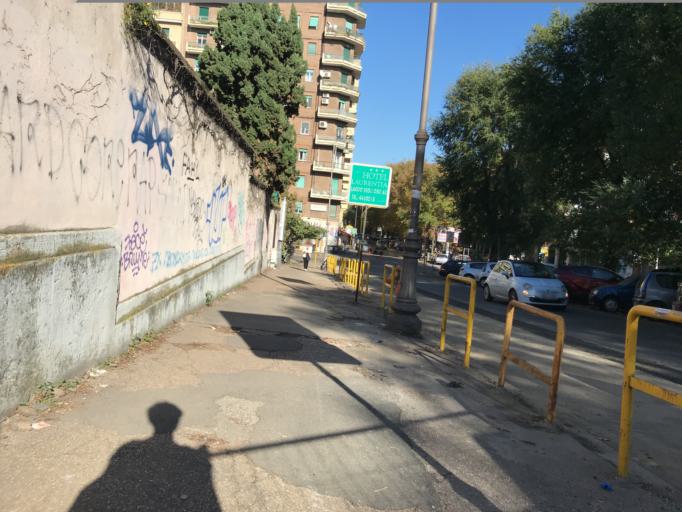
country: IT
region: Latium
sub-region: Citta metropolitana di Roma Capitale
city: Rome
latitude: 41.9059
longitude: 12.5160
